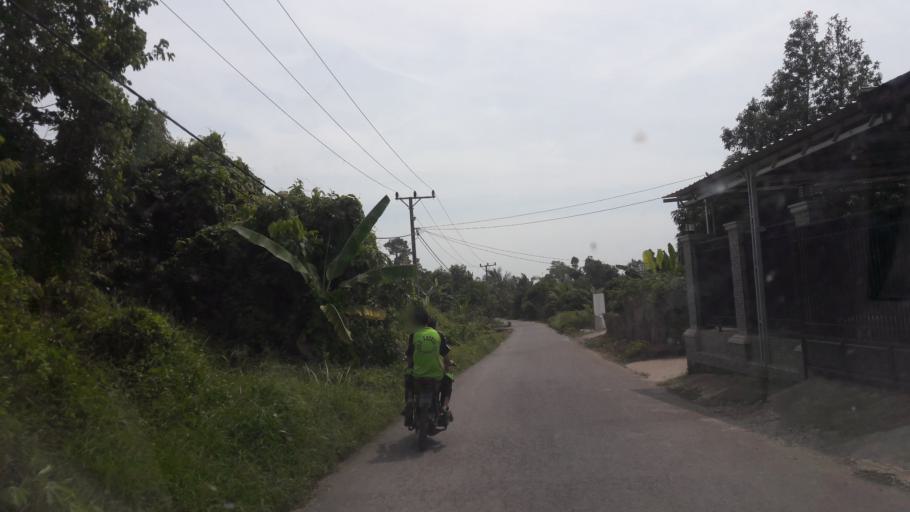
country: ID
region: South Sumatra
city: Gunungmenang
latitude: -3.1398
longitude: 104.1136
